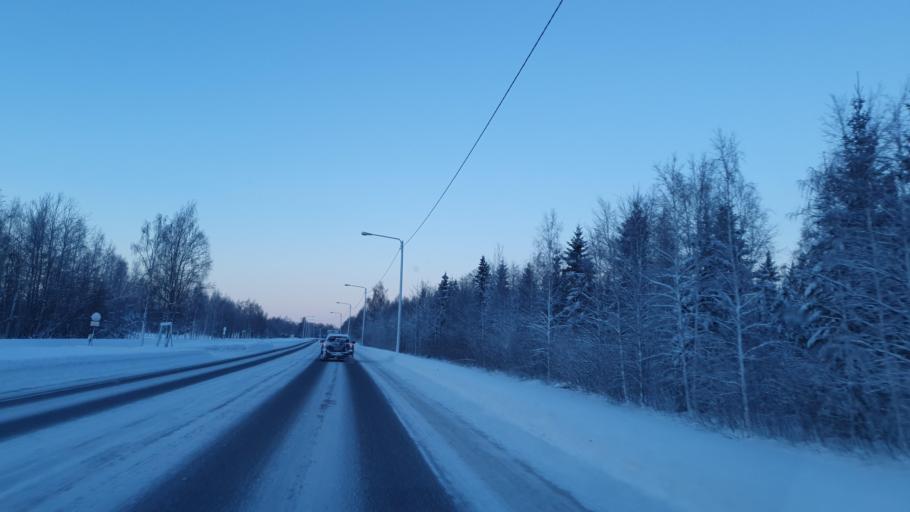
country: FI
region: Lapland
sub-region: Kemi-Tornio
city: Tornio
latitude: 65.8738
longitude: 24.1640
